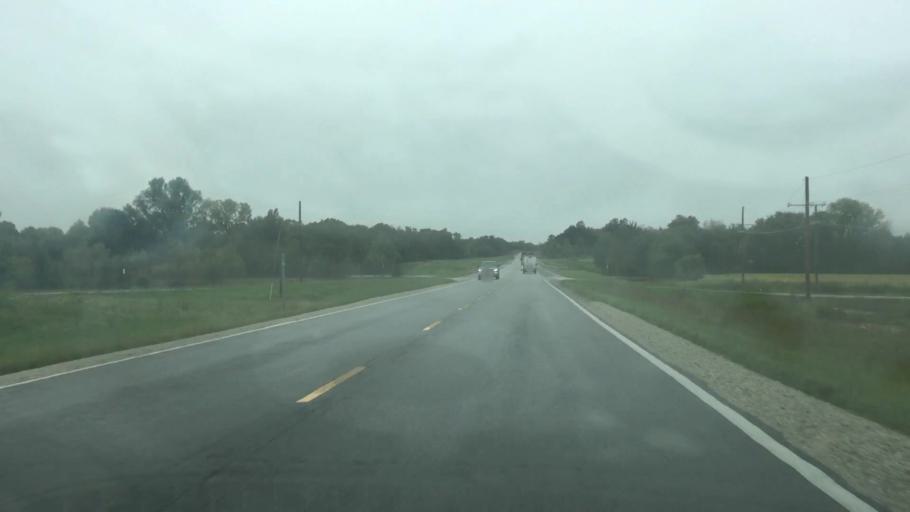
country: US
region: Kansas
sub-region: Anderson County
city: Garnett
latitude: 38.2133
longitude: -95.2488
